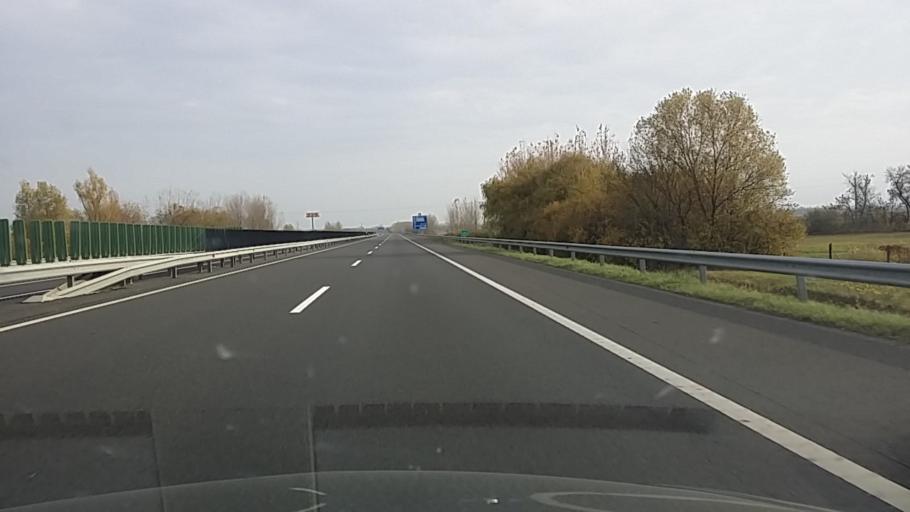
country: HU
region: Szabolcs-Szatmar-Bereg
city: Nyiregyhaza
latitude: 47.8908
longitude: 21.6910
